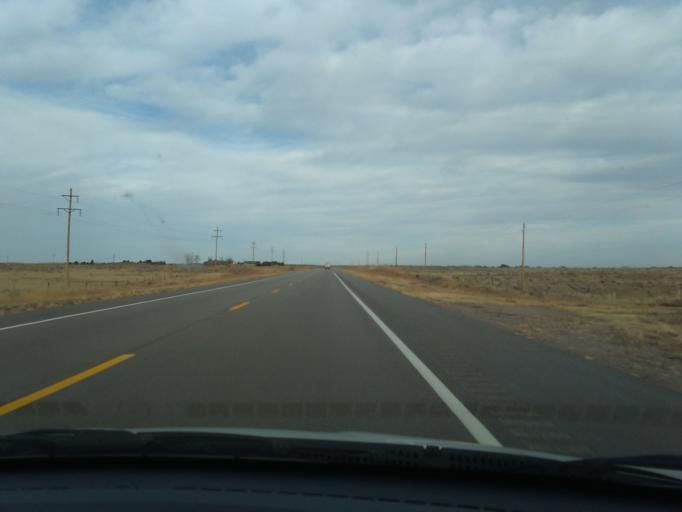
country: US
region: Nebraska
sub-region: Dundy County
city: Benkelman
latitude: 40.0650
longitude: -101.5265
